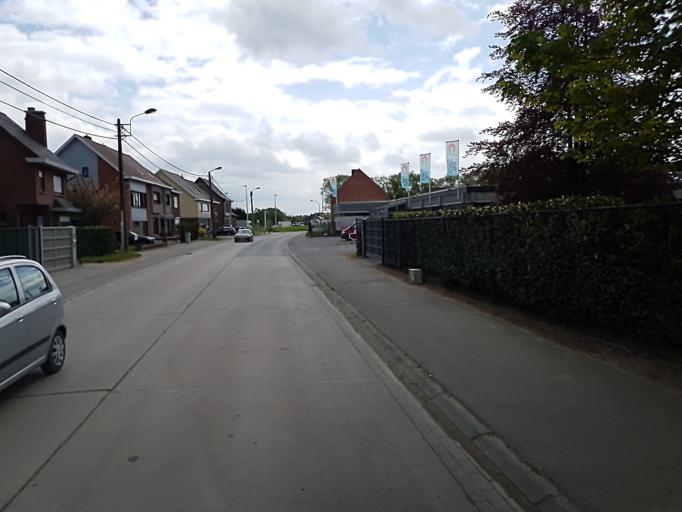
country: BE
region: Flanders
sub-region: Provincie Vlaams-Brabant
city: Londerzeel
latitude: 50.9989
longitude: 4.3139
